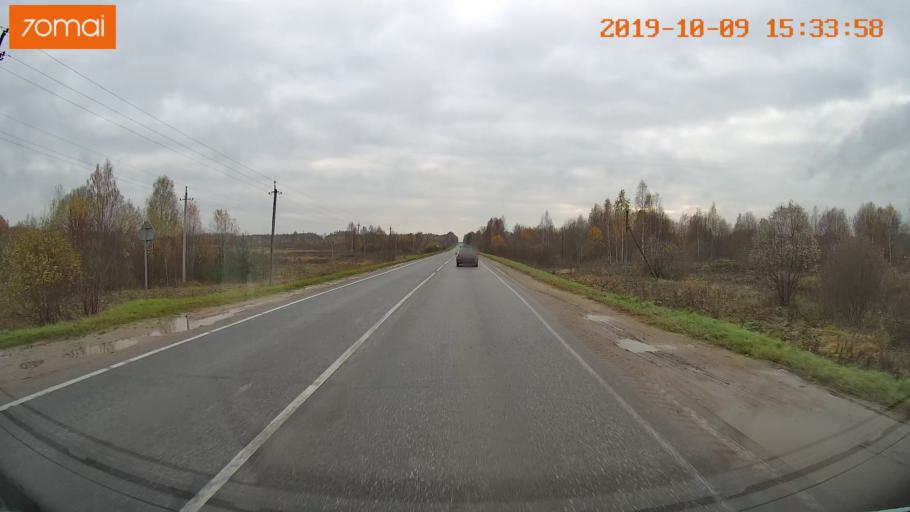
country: RU
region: Kostroma
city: Oktyabr'skiy
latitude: 57.9454
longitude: 41.2541
